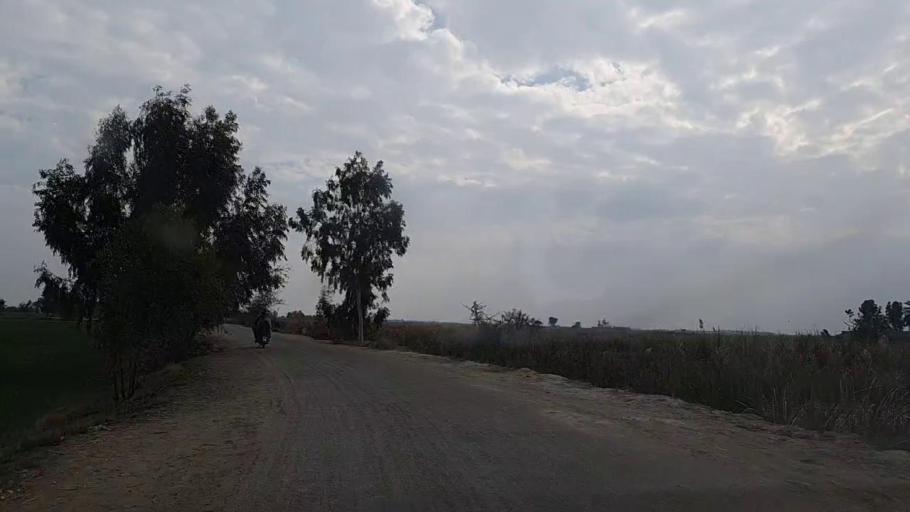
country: PK
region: Sindh
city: Sanghar
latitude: 26.2283
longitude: 69.0214
